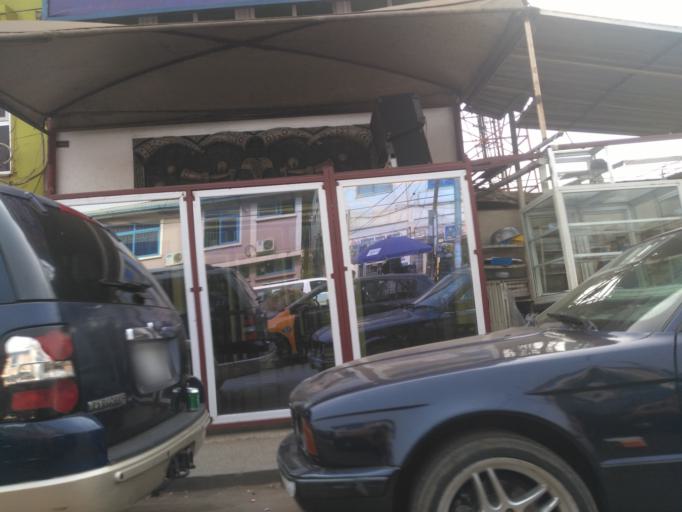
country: GH
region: Ashanti
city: Kumasi
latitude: 6.6864
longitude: -1.6152
